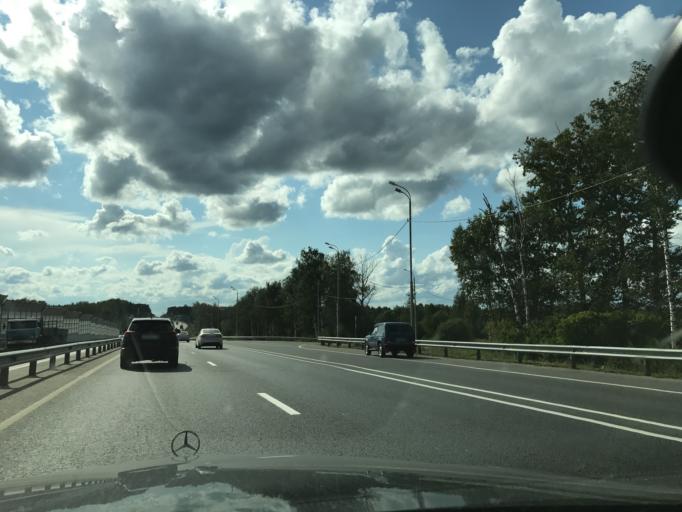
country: RU
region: Vladimir
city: Lakinsk
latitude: 56.0005
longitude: 39.9097
